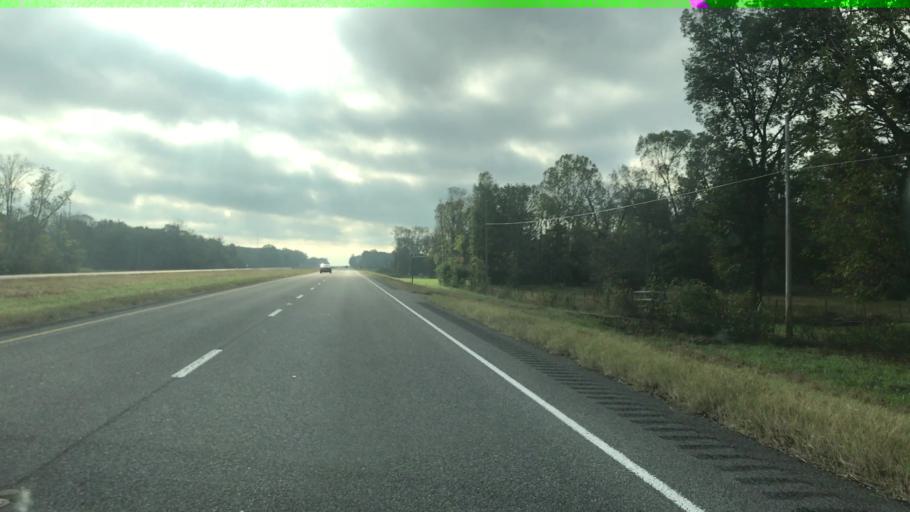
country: US
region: Alabama
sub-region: Morgan County
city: Danville
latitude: 34.4092
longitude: -87.1479
